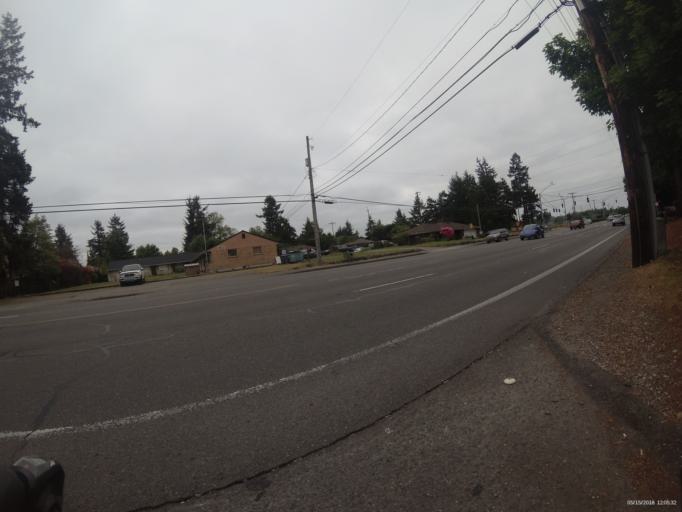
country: US
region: Washington
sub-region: Pierce County
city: Lakewood
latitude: 47.1796
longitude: -122.5522
